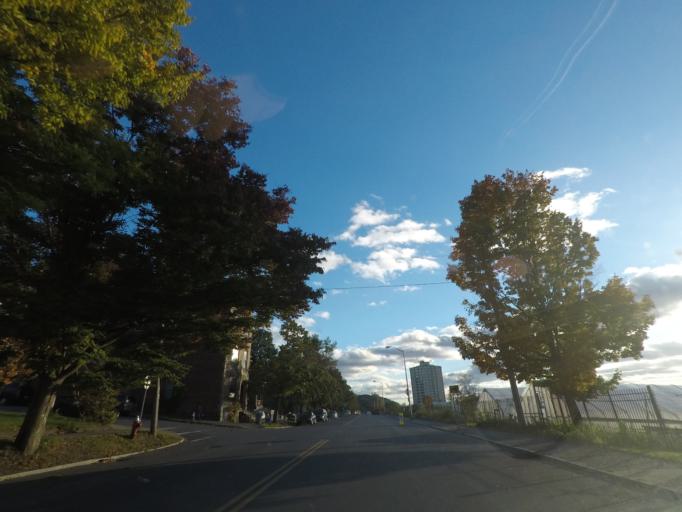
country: US
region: New York
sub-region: Albany County
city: Green Island
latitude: 42.7377
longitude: -73.6823
